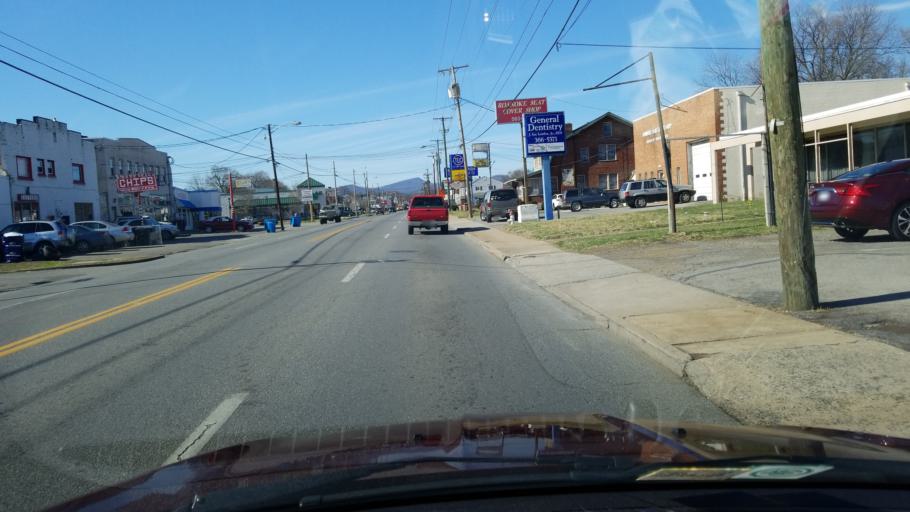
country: US
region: Virginia
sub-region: City of Roanoke
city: Roanoke
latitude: 37.2973
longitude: -79.9384
